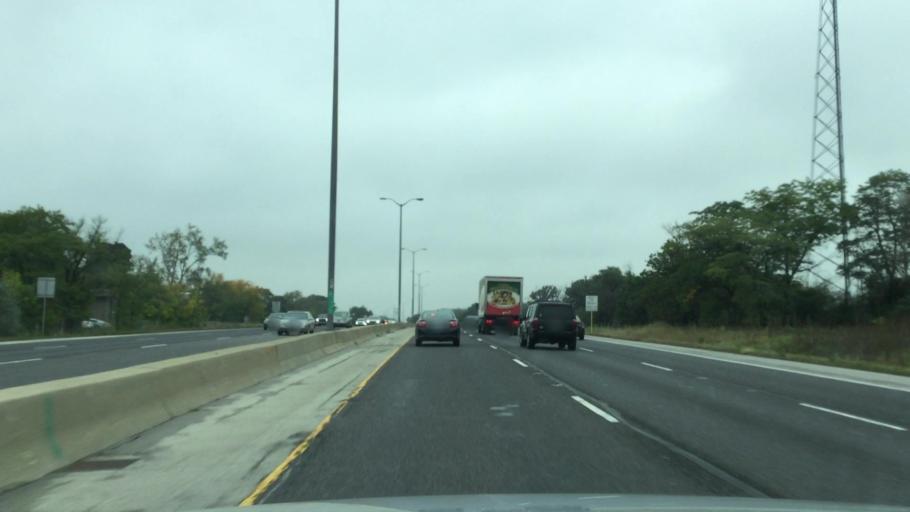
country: US
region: Illinois
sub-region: Cook County
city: Northfield
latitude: 42.1028
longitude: -87.7685
